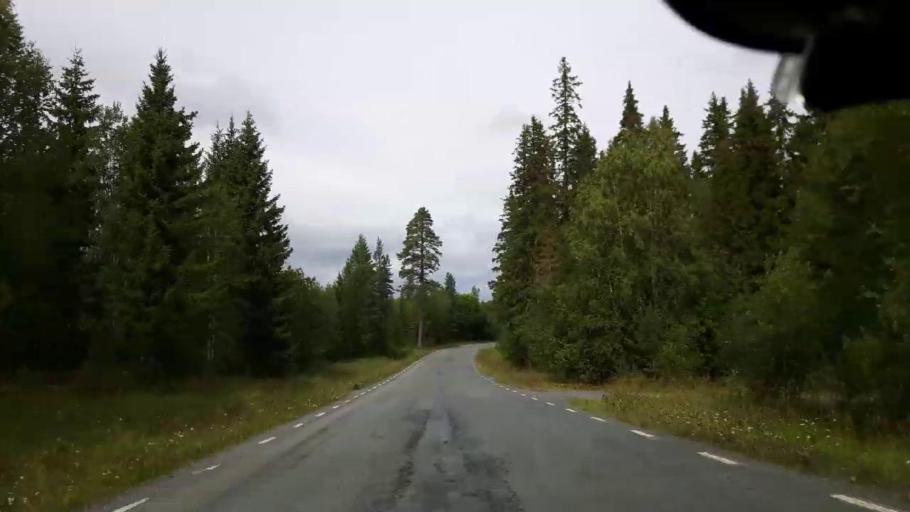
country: SE
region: Jaemtland
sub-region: Krokoms Kommun
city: Valla
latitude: 63.4708
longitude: 14.0087
